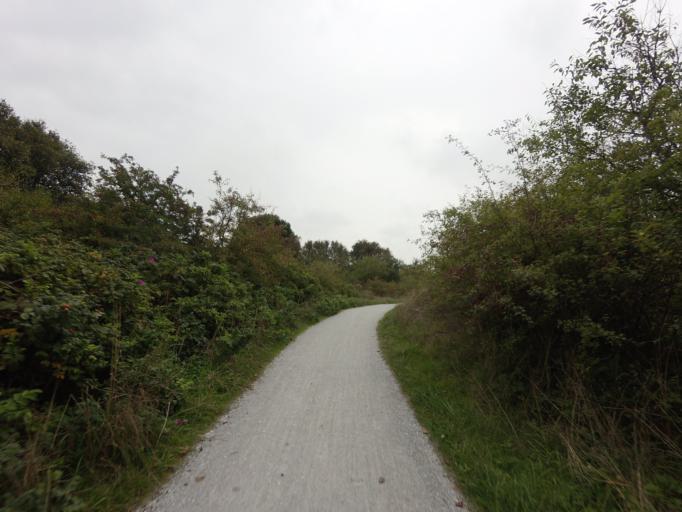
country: NL
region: Friesland
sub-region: Gemeente Schiermonnikoog
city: Schiermonnikoog
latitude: 53.4842
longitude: 6.1597
